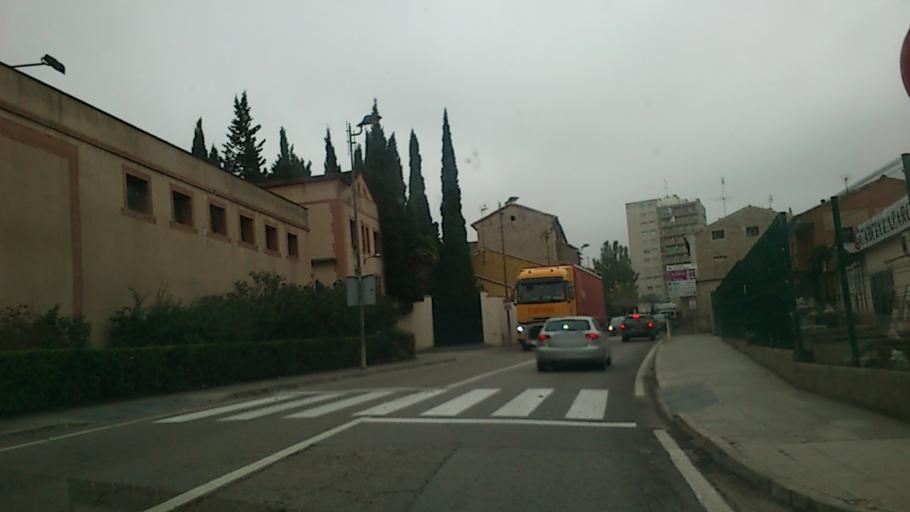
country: ES
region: Aragon
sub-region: Provincia de Zaragoza
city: Borja
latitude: 41.8324
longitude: -1.5263
